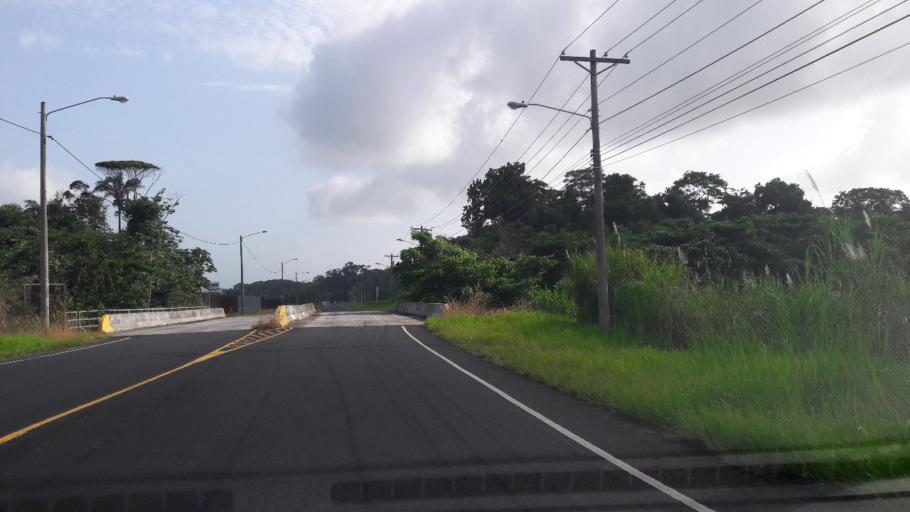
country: PA
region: Colon
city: Cativa
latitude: 9.3566
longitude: -79.8632
